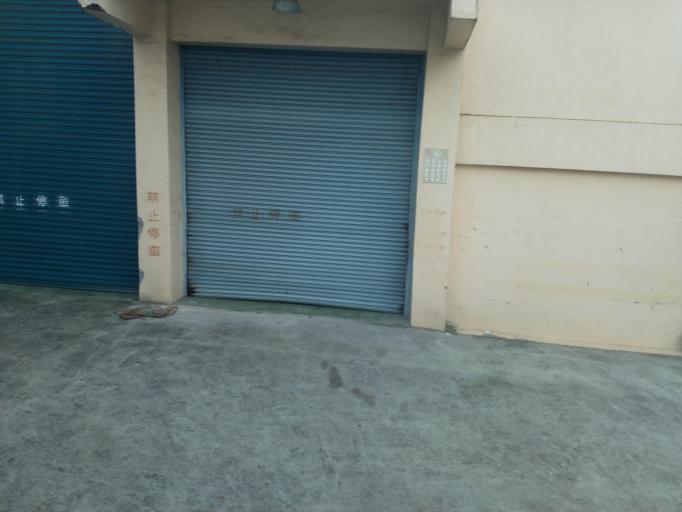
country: TW
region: Taiwan
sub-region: Pingtung
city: Pingtung
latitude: 22.8714
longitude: 120.5367
